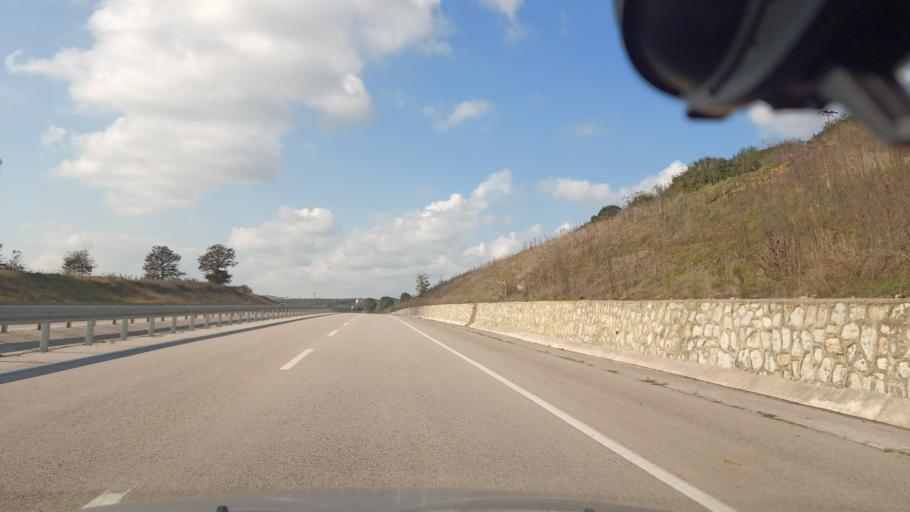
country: TR
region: Sakarya
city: Kaynarca
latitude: 41.0723
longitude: 30.3865
